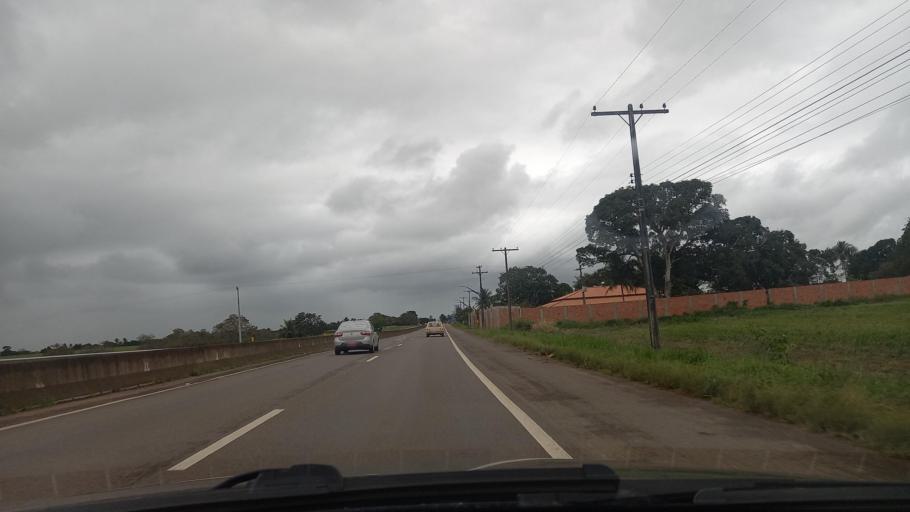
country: BR
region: Alagoas
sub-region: Limoeiro De Anadia
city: Cajueiro
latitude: -9.7498
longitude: -36.4553
